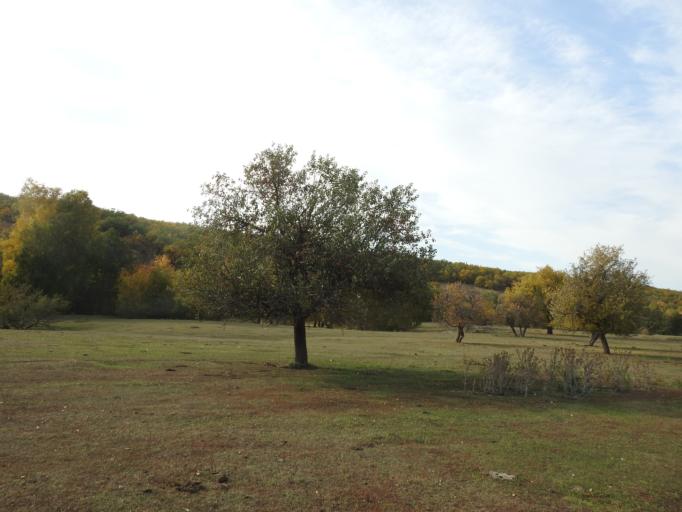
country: RU
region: Saratov
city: Baltay
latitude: 52.5407
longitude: 46.6542
